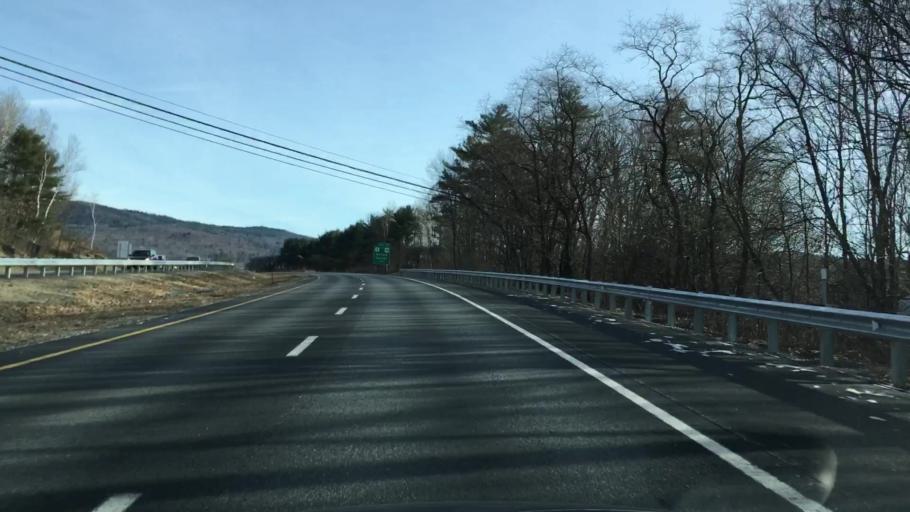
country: US
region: New Hampshire
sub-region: Grafton County
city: Lebanon
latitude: 43.6422
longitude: -72.2286
